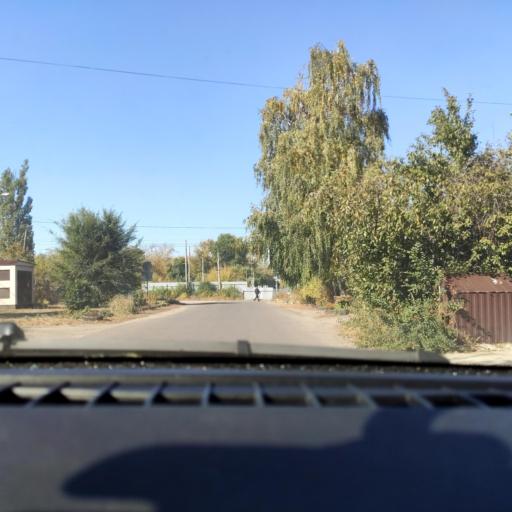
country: RU
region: Voronezj
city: Maslovka
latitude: 51.6168
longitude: 39.2593
